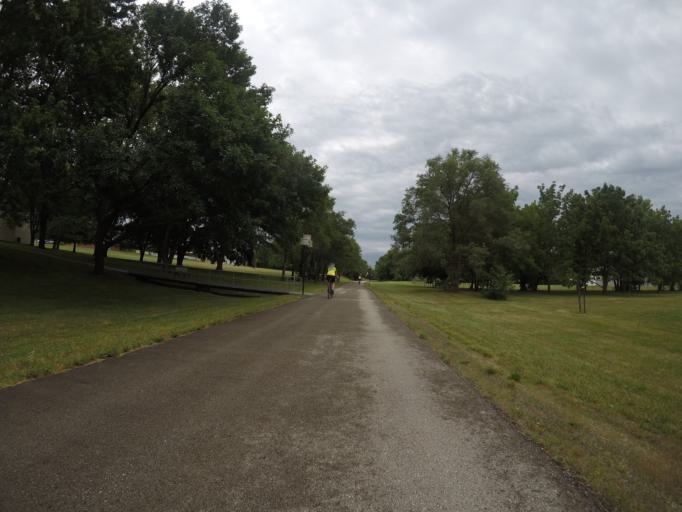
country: US
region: Kansas
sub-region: Anderson County
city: Garnett
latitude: 38.2858
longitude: -95.2405
